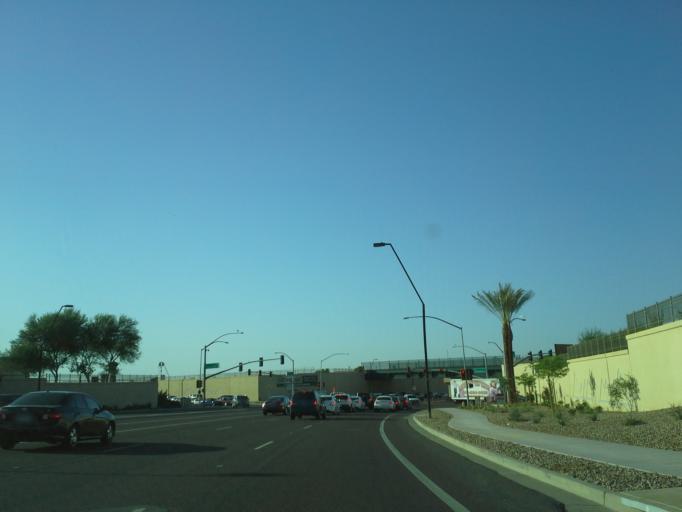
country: US
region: Arizona
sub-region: Maricopa County
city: Queen Creek
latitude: 33.2570
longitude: -111.6383
